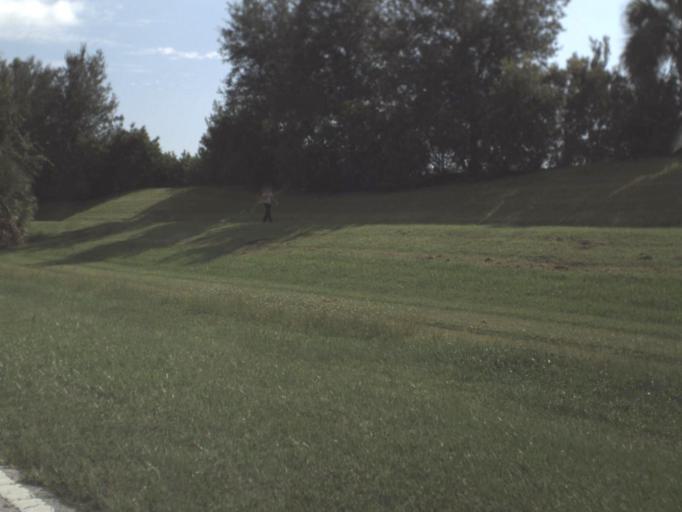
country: US
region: Florida
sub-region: Sarasota County
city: Plantation
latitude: 27.0886
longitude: -82.3368
